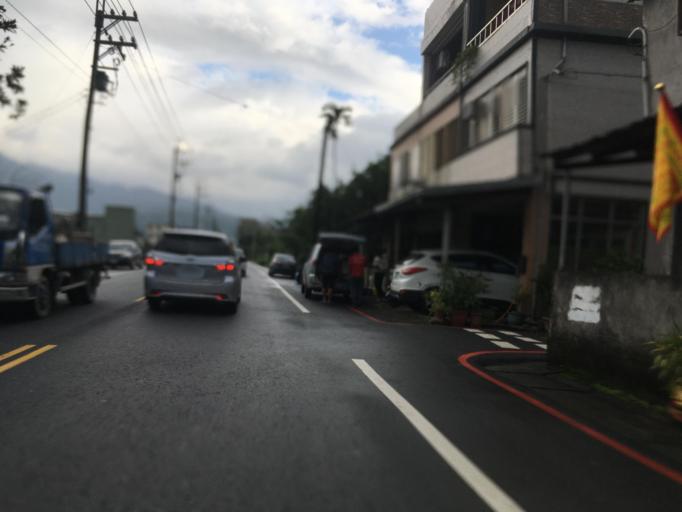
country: TW
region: Taiwan
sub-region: Yilan
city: Yilan
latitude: 24.8395
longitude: 121.8057
